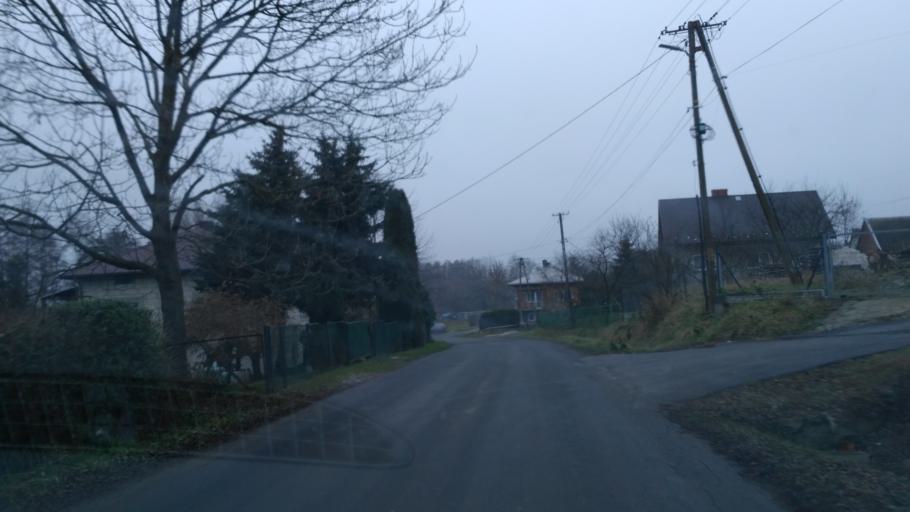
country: PL
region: Subcarpathian Voivodeship
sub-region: Powiat przeworski
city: Zarzecze
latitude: 49.9642
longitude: 22.5664
